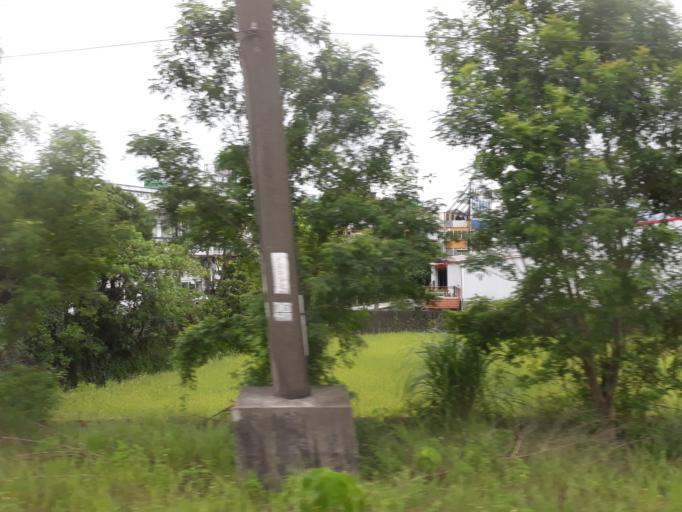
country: TW
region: Taiwan
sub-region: Yilan
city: Yilan
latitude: 24.7093
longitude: 121.7735
